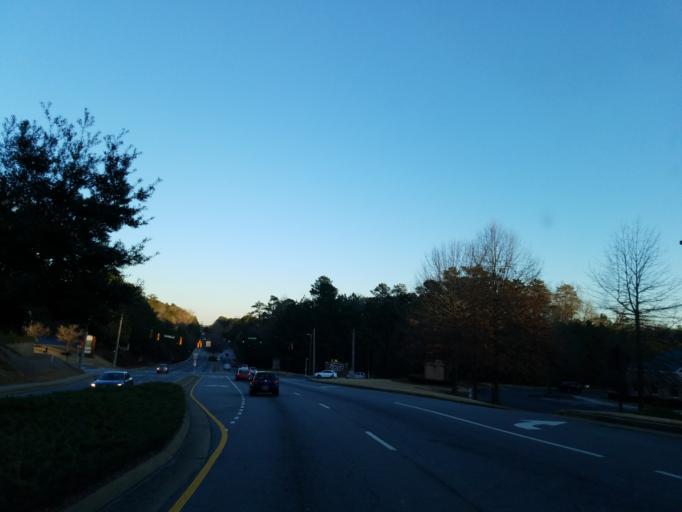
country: US
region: Georgia
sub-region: Cherokee County
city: Woodstock
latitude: 34.1088
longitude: -84.5517
